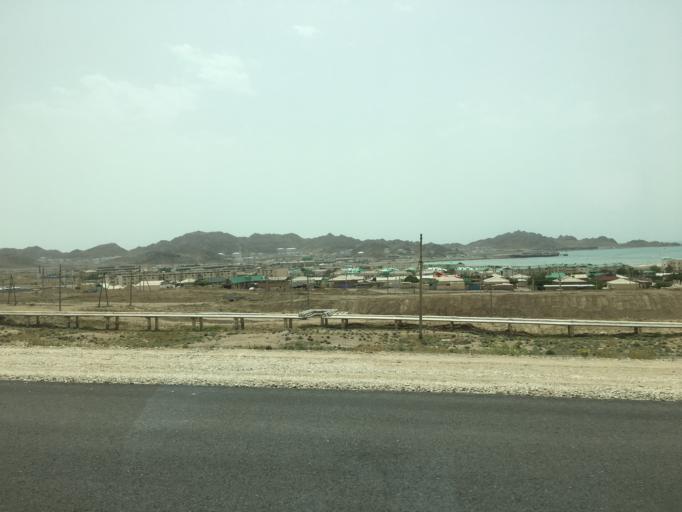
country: TM
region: Balkan
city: Turkmenbasy
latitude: 40.0133
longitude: 53.0676
